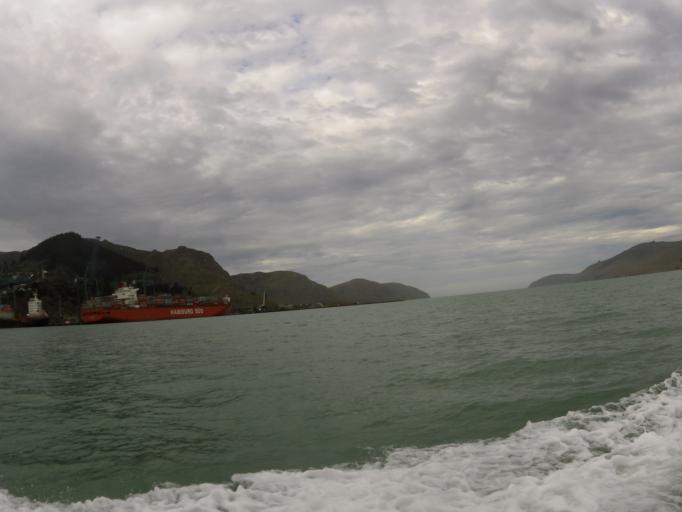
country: NZ
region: Canterbury
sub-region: Christchurch City
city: Christchurch
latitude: -43.6139
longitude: 172.7224
